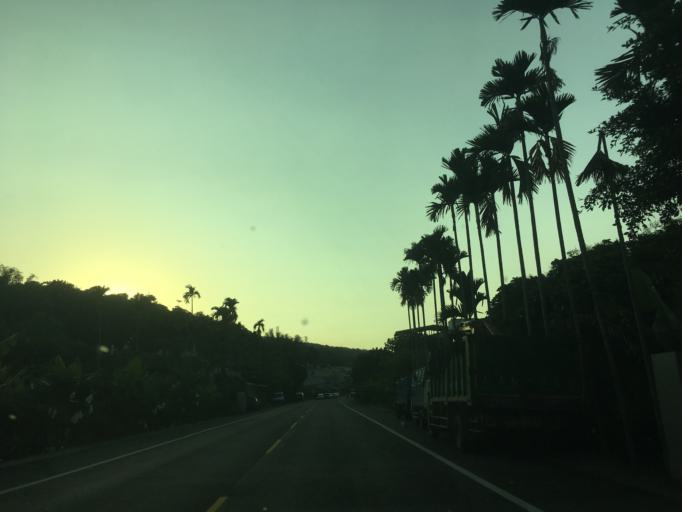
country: TW
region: Taiwan
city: Zhongxing New Village
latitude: 23.9495
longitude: 120.6595
